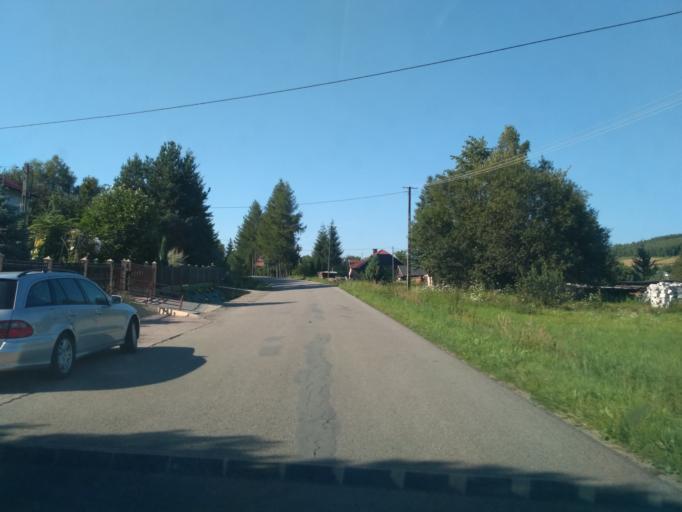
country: PL
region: Subcarpathian Voivodeship
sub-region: Powiat strzyzowski
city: Wysoka Strzyzowska
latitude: 49.8073
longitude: 21.7461
